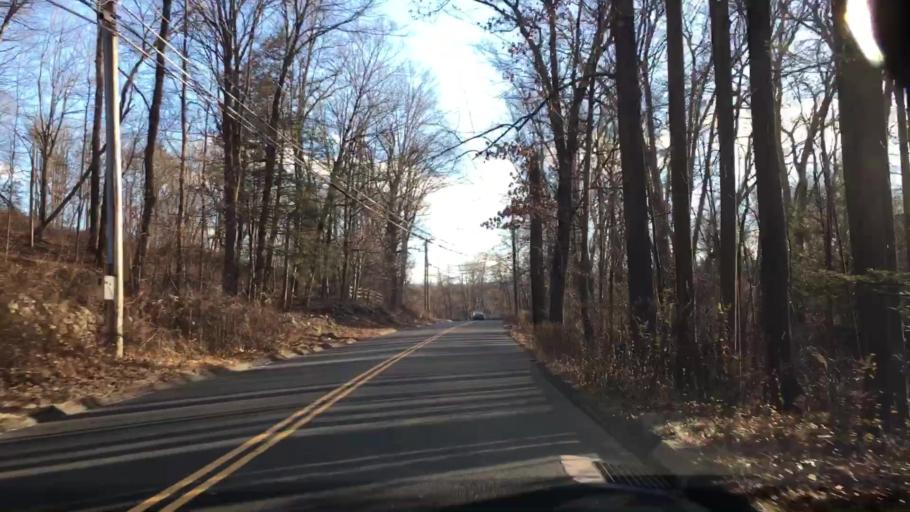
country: US
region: Connecticut
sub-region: Fairfield County
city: Newtown
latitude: 41.4318
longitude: -73.3151
